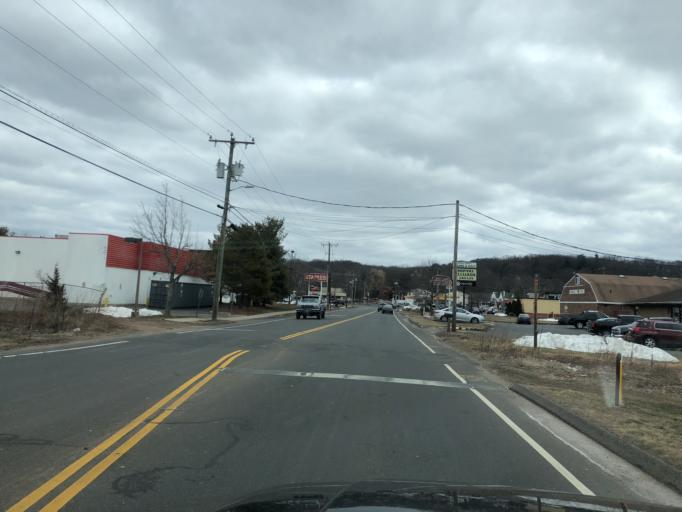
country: US
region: Connecticut
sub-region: Hartford County
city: Plainville
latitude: 41.6341
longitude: -72.8764
